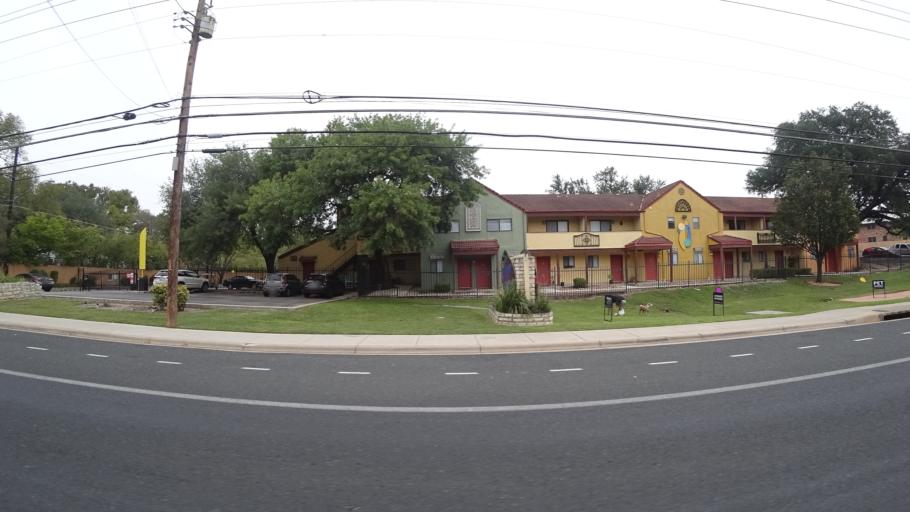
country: US
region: Texas
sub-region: Travis County
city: Austin
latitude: 30.2201
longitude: -97.7710
